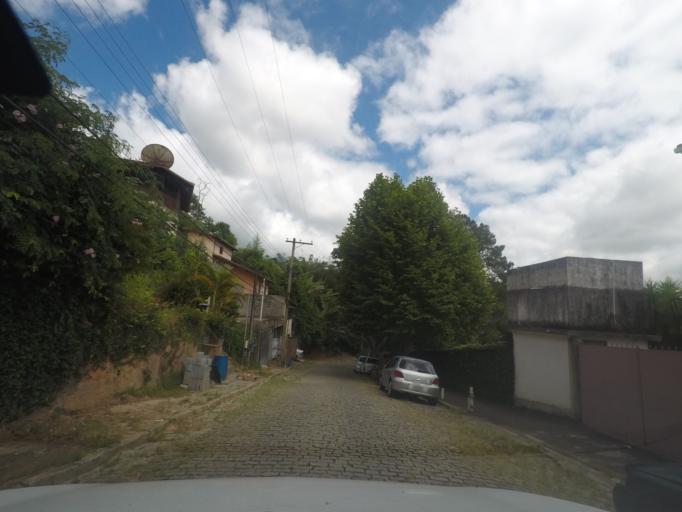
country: BR
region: Rio de Janeiro
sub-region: Teresopolis
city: Teresopolis
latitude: -22.3975
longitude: -42.9858
